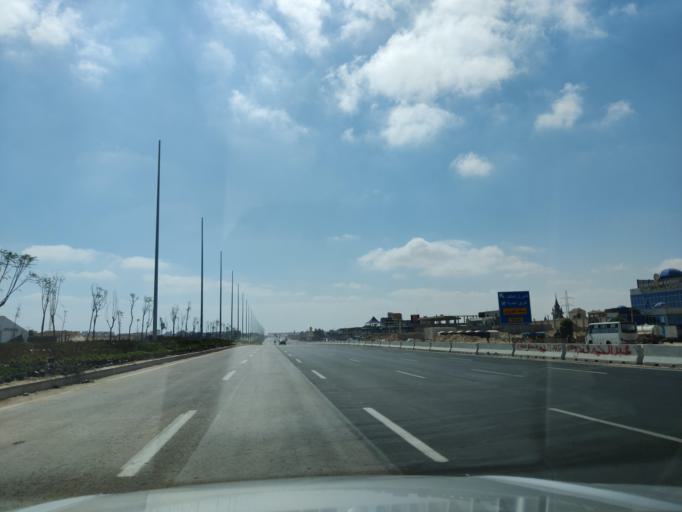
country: EG
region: Muhafazat Matruh
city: Al `Alamayn
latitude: 30.9916
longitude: 28.6768
